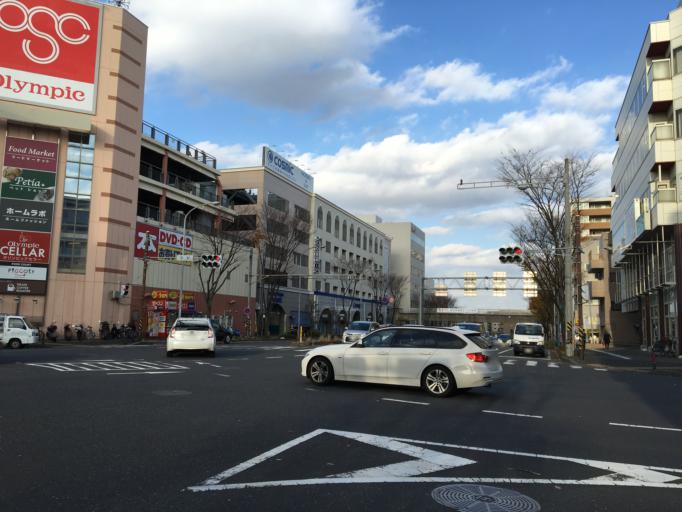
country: JP
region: Tokyo
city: Chofugaoka
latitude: 35.5429
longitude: 139.5698
